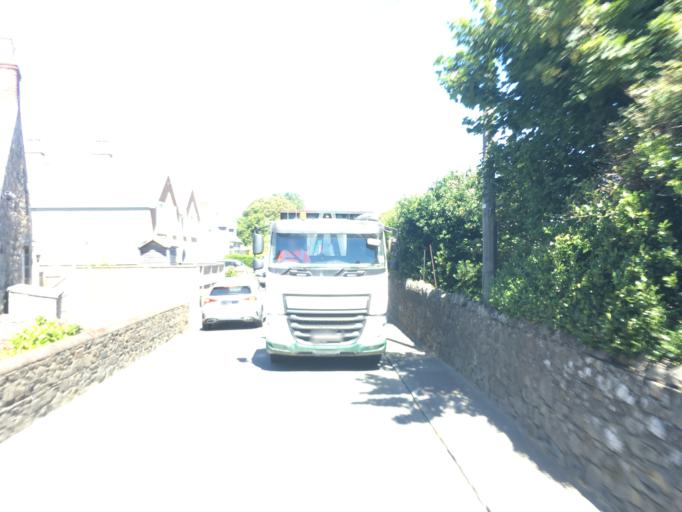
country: GG
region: St Peter Port
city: Saint Peter Port
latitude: 49.4910
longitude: -2.5085
